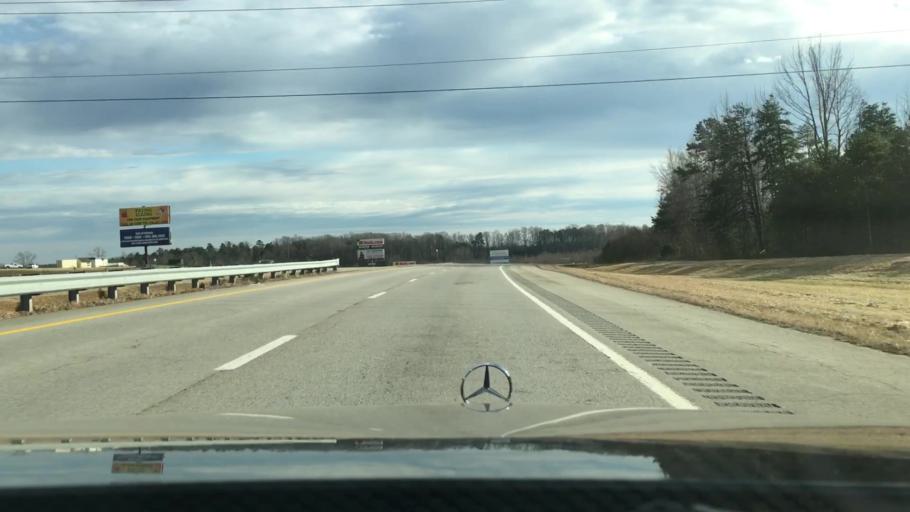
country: US
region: Virginia
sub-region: Pittsylvania County
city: Mount Hermon
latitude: 36.6966
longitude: -79.3625
